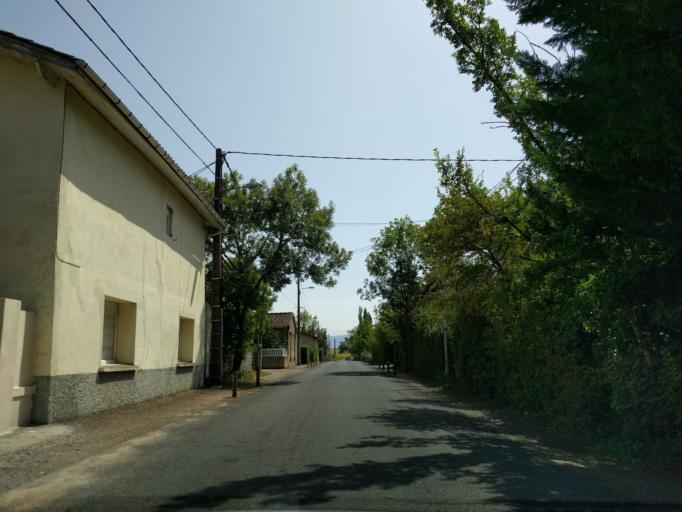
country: FR
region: Midi-Pyrenees
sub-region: Departement du Tarn
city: Castres
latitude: 43.5884
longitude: 2.2601
